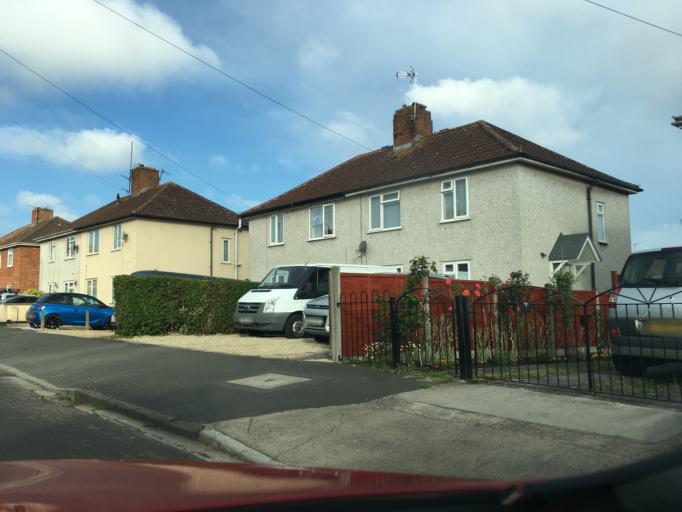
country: GB
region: England
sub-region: North Somerset
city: Easton-in-Gordano
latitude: 51.4928
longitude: -2.6840
